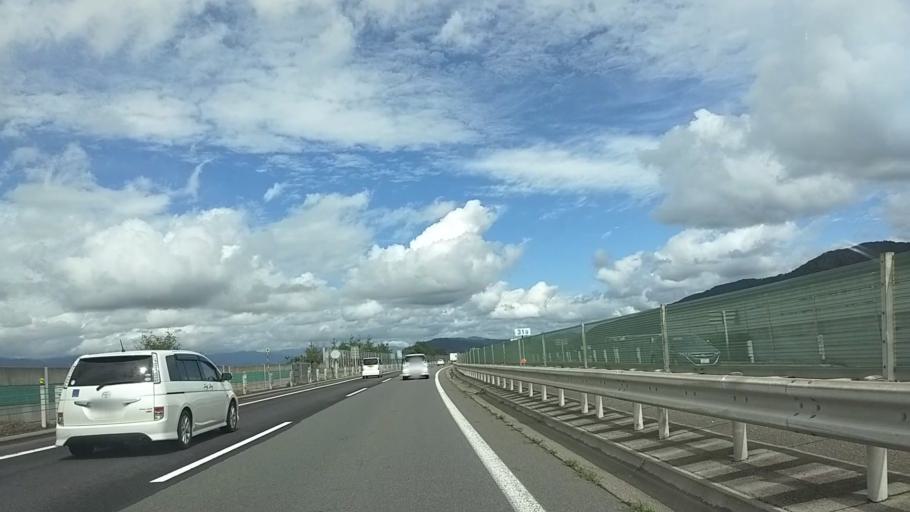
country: JP
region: Nagano
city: Toyoshina
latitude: 36.2877
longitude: 137.9284
